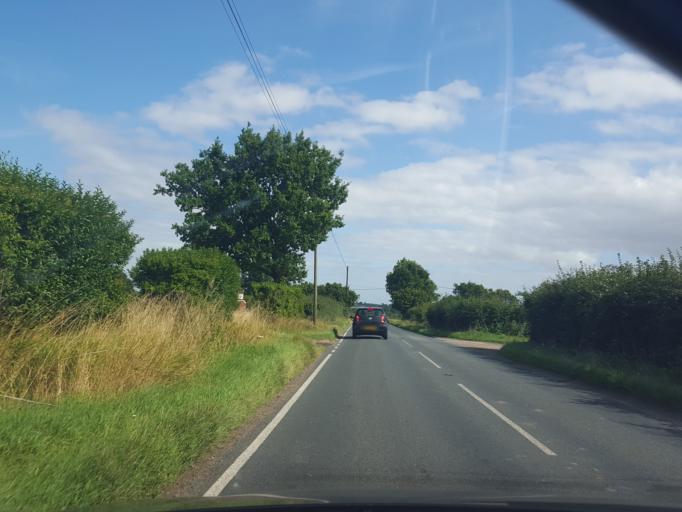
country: GB
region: England
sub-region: Suffolk
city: Shotley Gate
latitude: 51.9345
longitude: 1.2087
